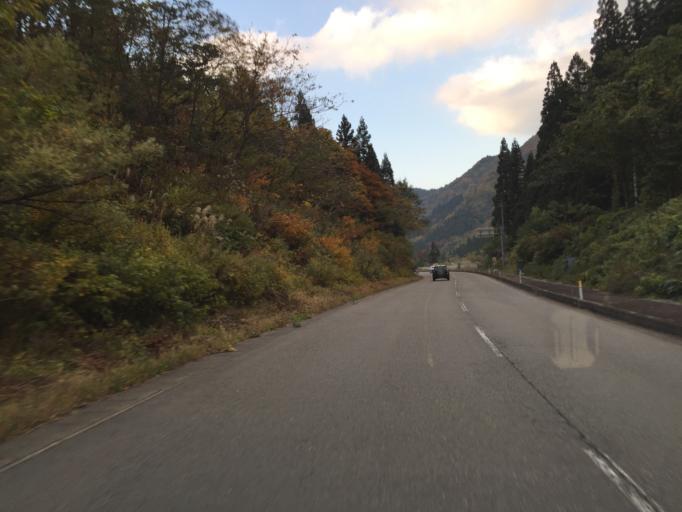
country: JP
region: Yamagata
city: Yonezawa
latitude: 37.8317
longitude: 140.0022
